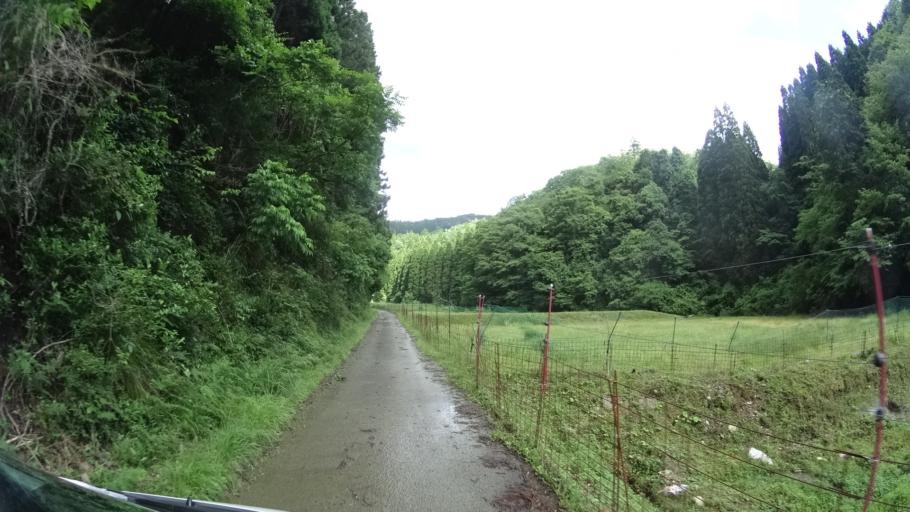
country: JP
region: Kyoto
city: Maizuru
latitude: 35.3913
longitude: 135.2708
